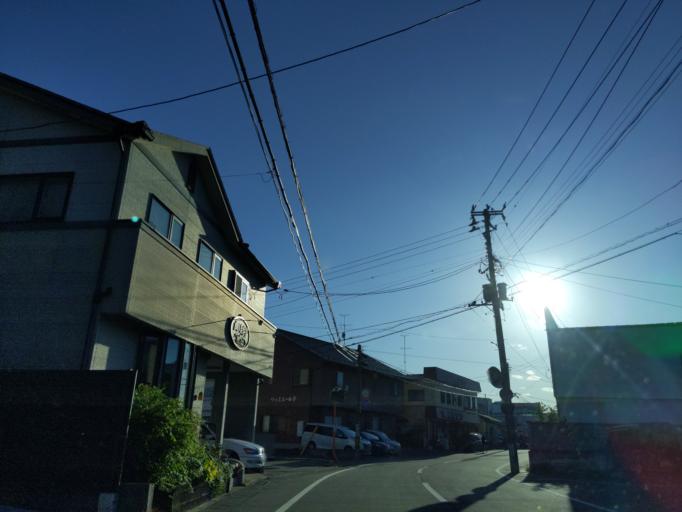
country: JP
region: Fukushima
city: Koriyama
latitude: 37.3934
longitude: 140.4002
